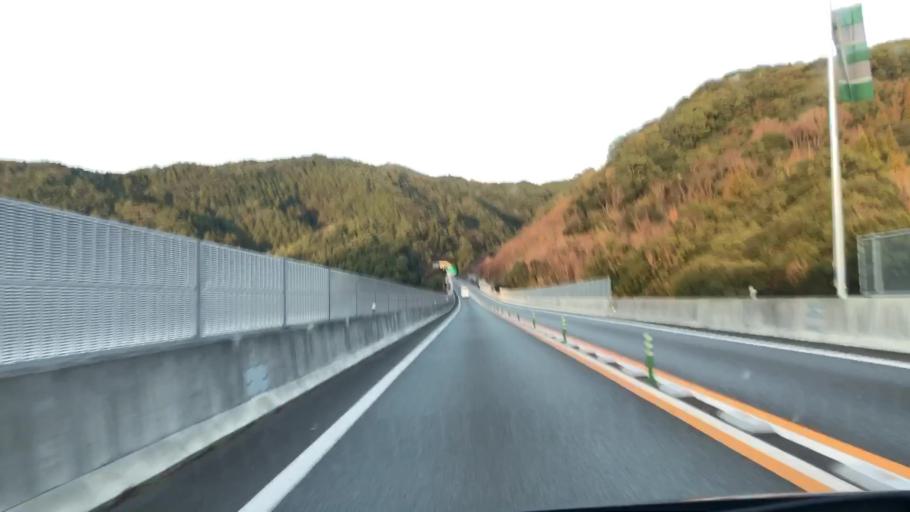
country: JP
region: Kumamoto
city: Minamata
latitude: 32.2794
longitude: 130.4984
